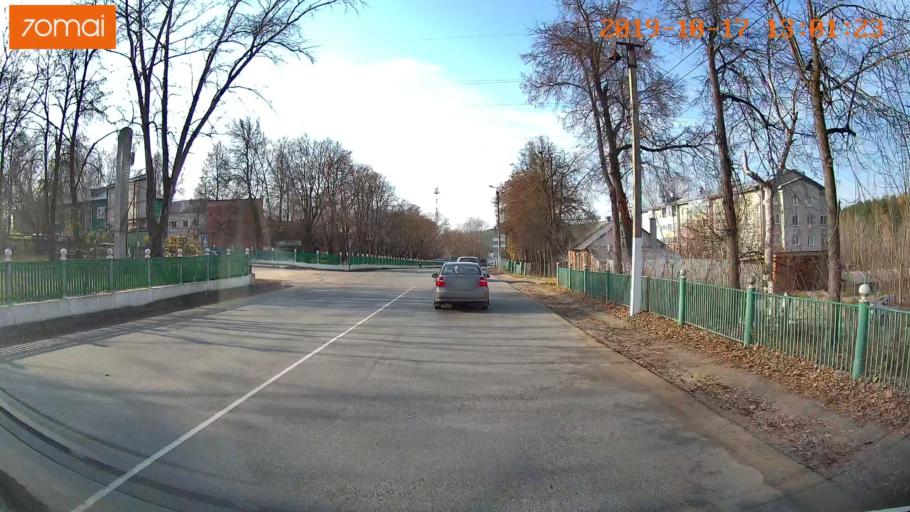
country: RU
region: Rjazan
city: Kasimov
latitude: 54.9457
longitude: 41.3709
